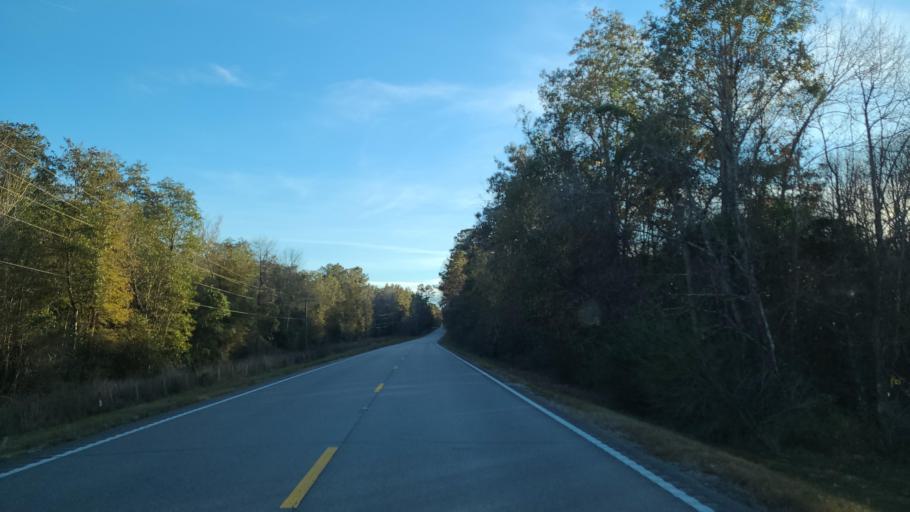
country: US
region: Mississippi
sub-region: Lamar County
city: Purvis
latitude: 31.0825
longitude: -89.4173
